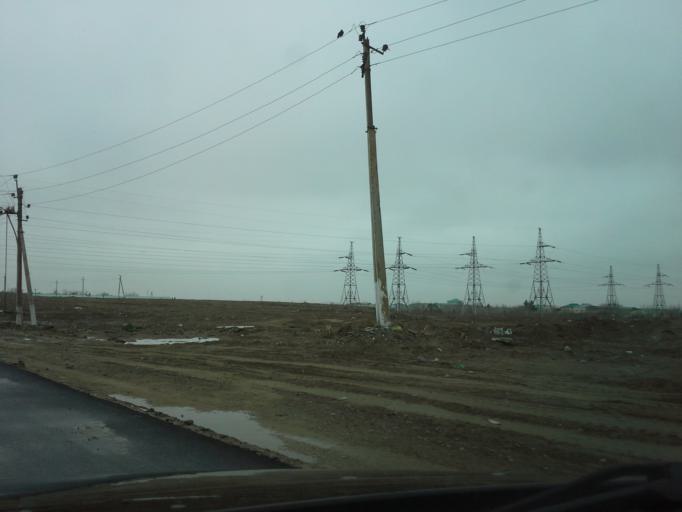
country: TM
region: Ahal
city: Ashgabat
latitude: 37.9576
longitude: 58.4262
